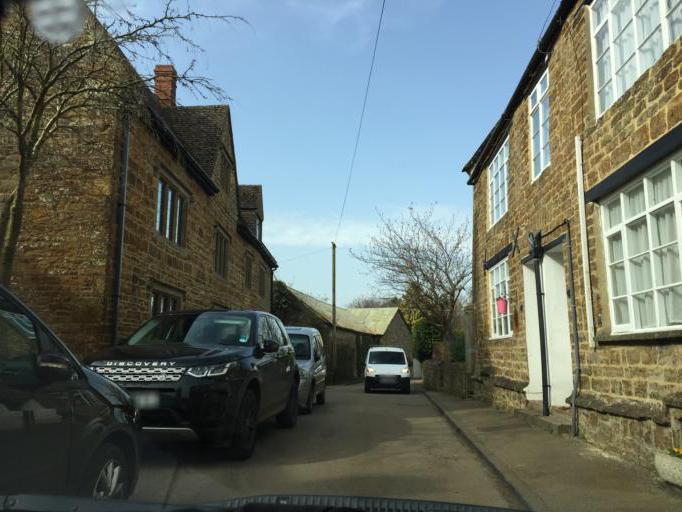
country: GB
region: England
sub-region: Oxfordshire
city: Banbury
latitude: 52.0748
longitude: -1.2744
